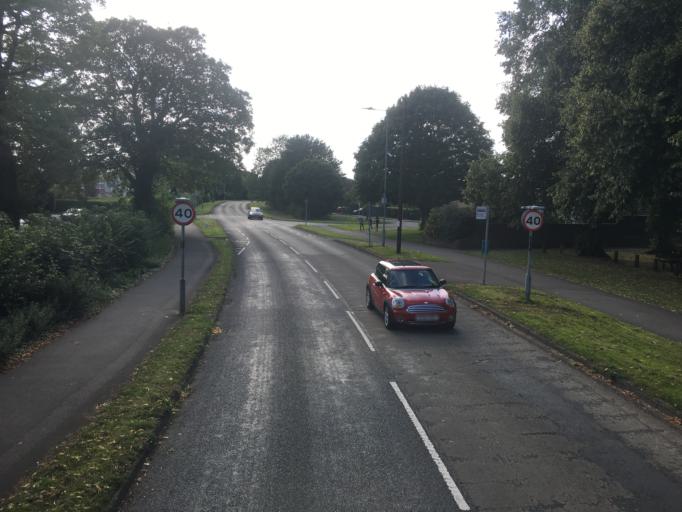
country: GB
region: England
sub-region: Leicestershire
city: Lutterworth
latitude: 52.4567
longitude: -1.2075
